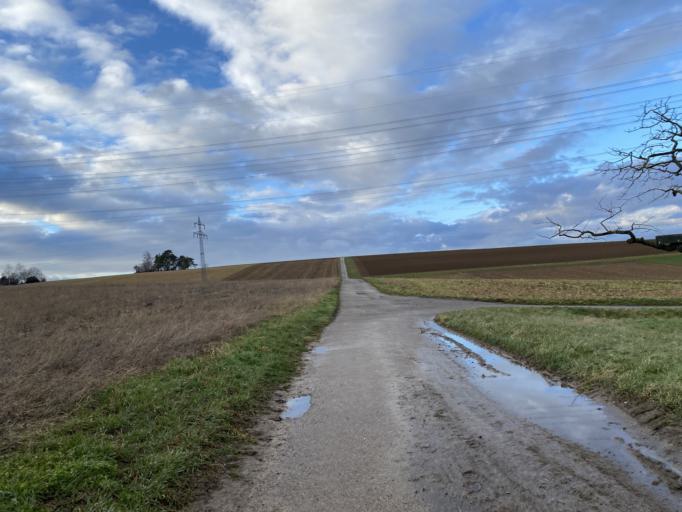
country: DE
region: Baden-Wuerttemberg
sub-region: Regierungsbezirk Stuttgart
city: Eberdingen
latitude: 48.9002
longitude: 8.9325
